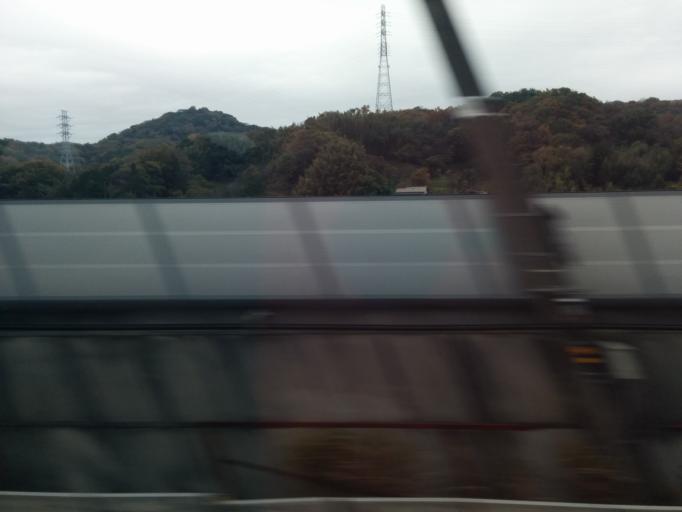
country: JP
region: Kanagawa
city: Oiso
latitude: 35.3232
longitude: 139.2868
